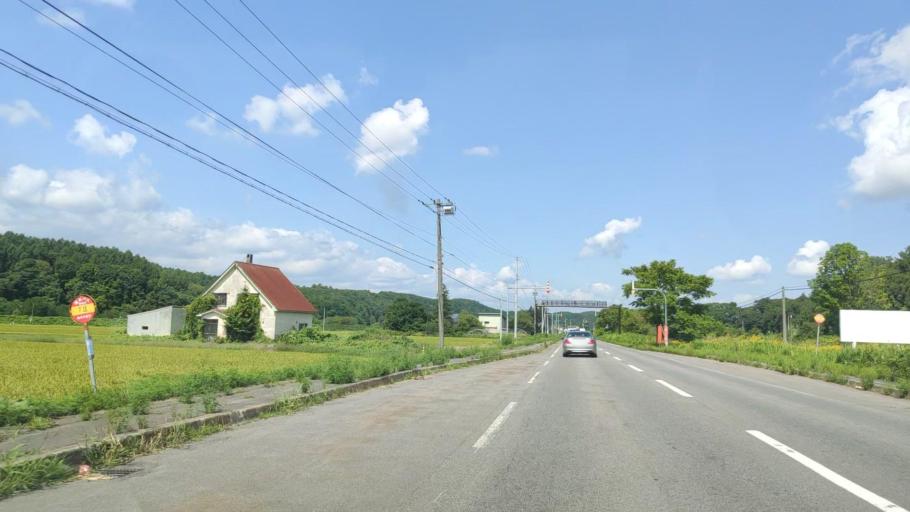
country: JP
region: Hokkaido
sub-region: Asahikawa-shi
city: Asahikawa
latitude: 43.6292
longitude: 142.4632
